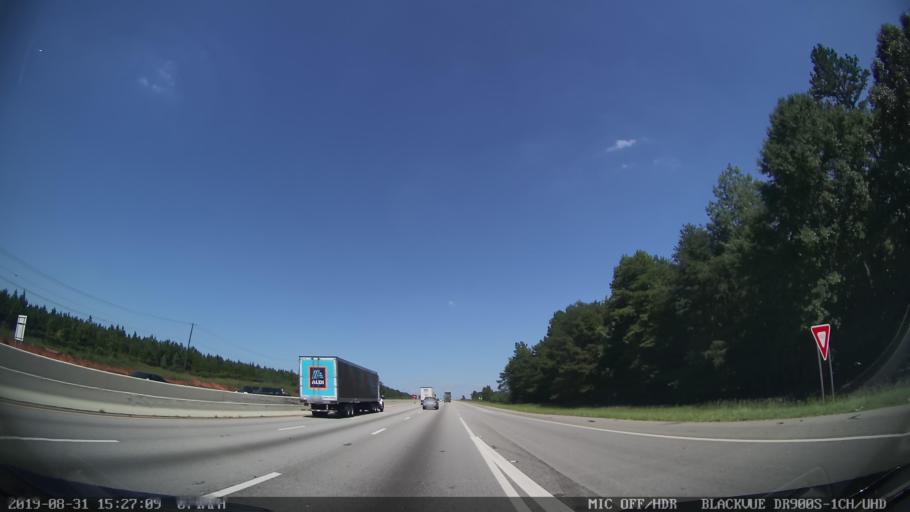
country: US
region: South Carolina
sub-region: Greenville County
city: Greer
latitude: 34.8786
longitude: -82.2089
